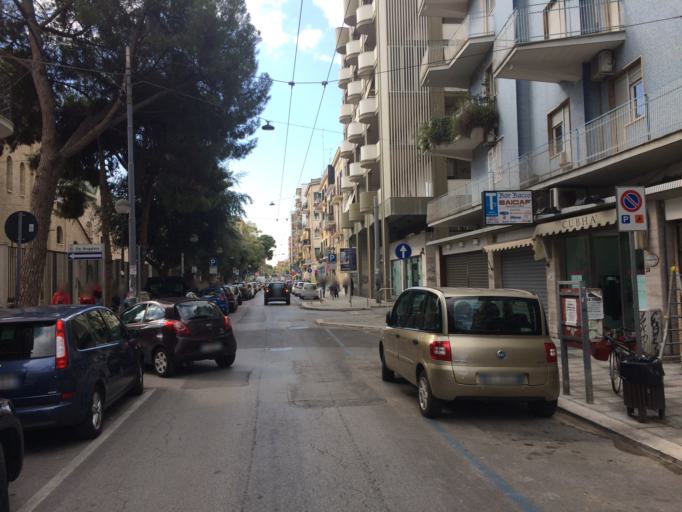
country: IT
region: Apulia
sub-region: Provincia di Bari
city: Bari
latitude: 41.1107
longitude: 16.8721
